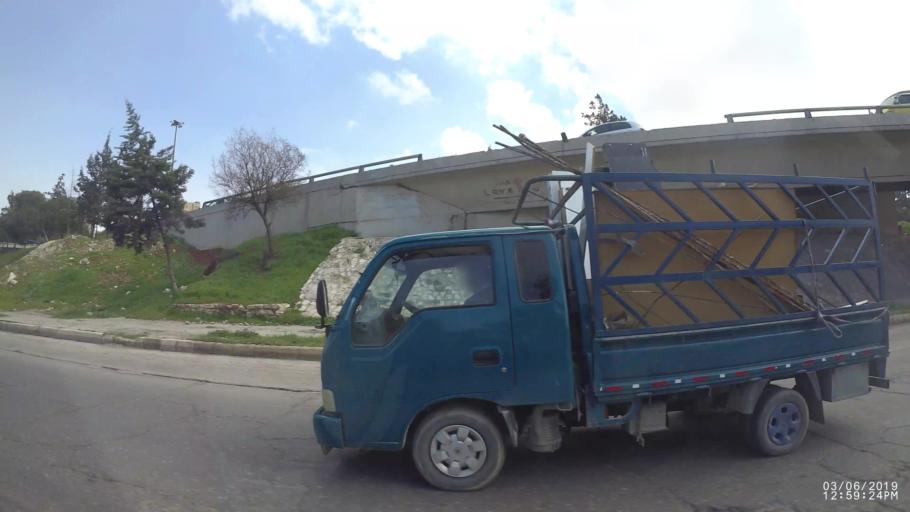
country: JO
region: Amman
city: Amman
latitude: 31.9902
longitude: 35.9785
